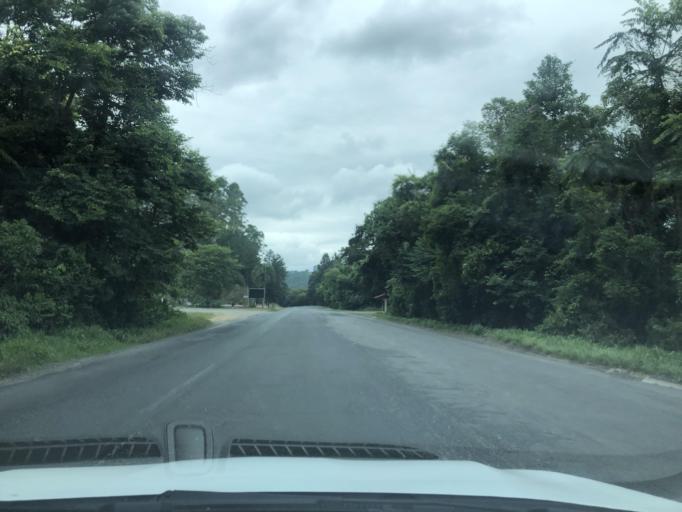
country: BR
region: Santa Catarina
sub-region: Rio Do Sul
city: Rio do Sul
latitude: -27.2808
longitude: -49.8197
